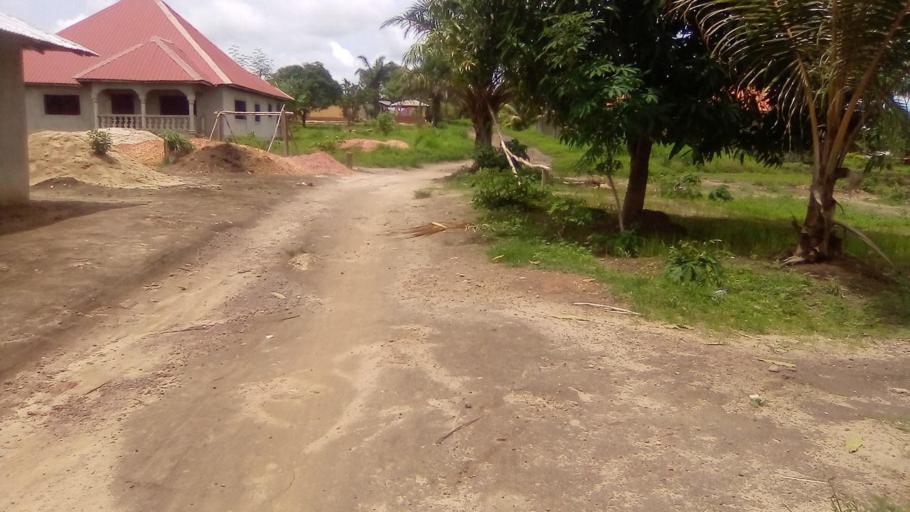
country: SL
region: Southern Province
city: Bo
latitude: 7.9380
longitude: -11.7408
